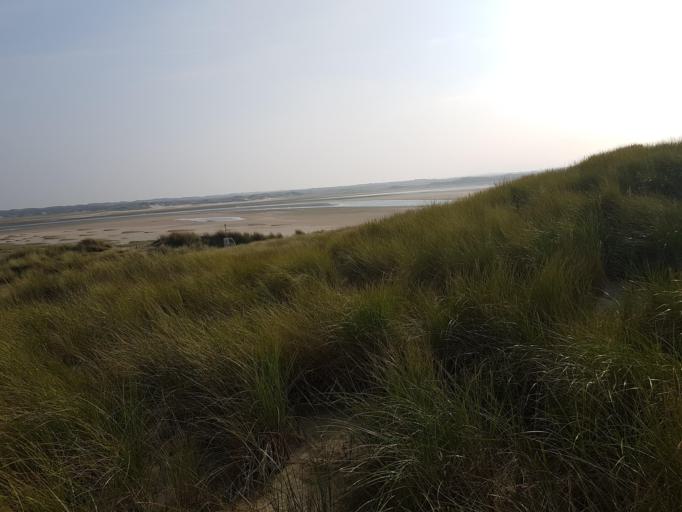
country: NL
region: North Holland
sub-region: Gemeente Texel
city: Den Burg
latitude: 53.1405
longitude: 4.8044
